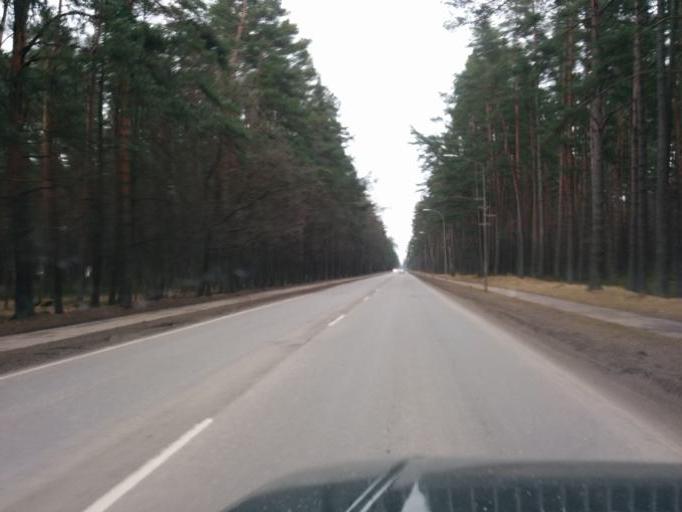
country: LV
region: Jurmala
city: Jurmala
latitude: 56.9570
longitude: 23.6518
